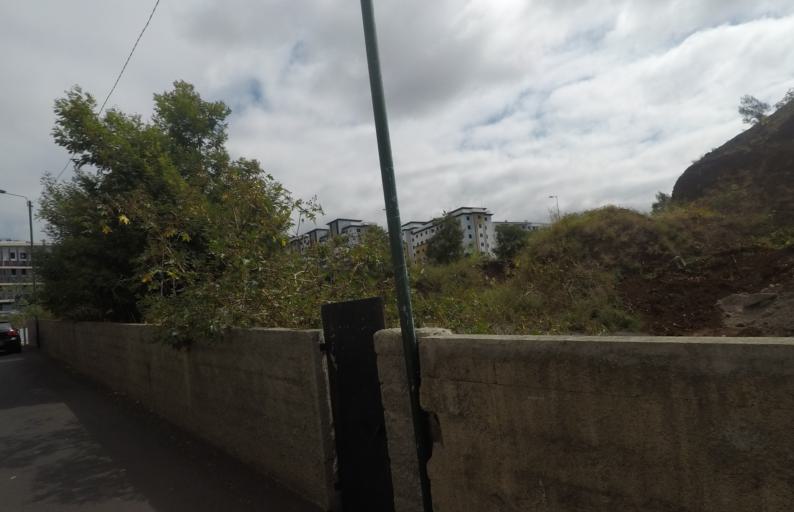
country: PT
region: Madeira
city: Camara de Lobos
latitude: 32.6471
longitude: -16.9403
